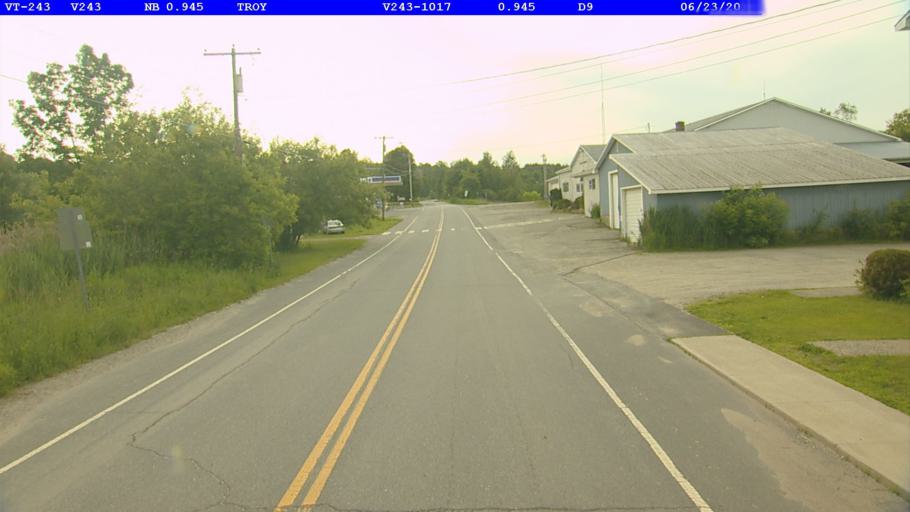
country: US
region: Vermont
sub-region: Orleans County
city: Newport
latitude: 44.9972
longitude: -72.4047
